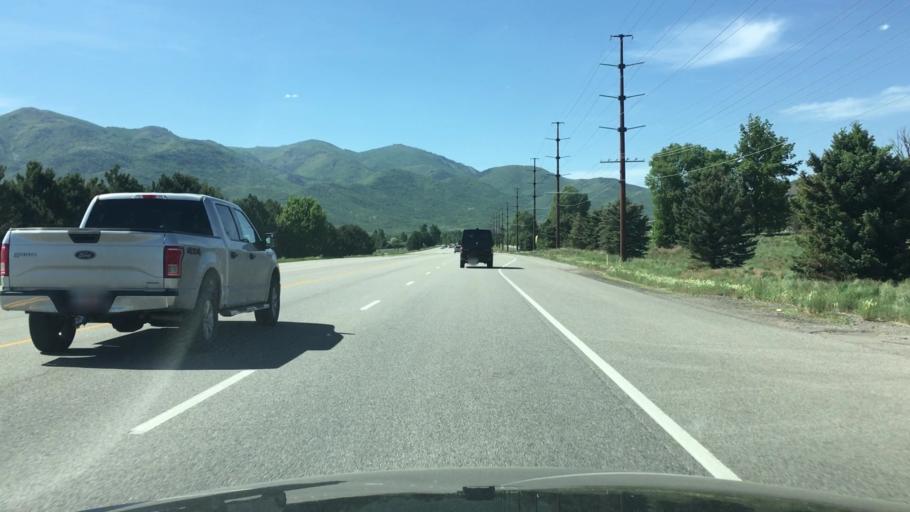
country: US
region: Utah
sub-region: Wasatch County
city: Heber
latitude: 40.5386
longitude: -111.4125
